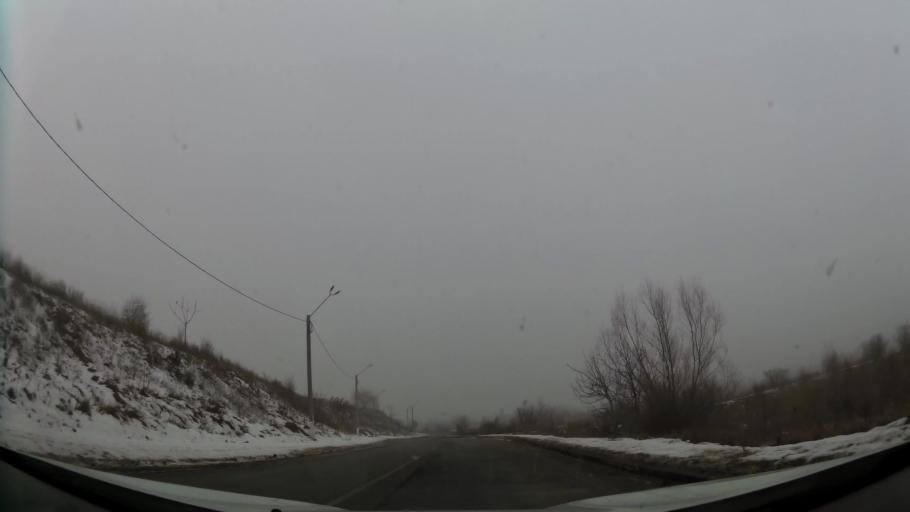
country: RO
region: Ilfov
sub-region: Comuna Chiajna
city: Chiajna
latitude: 44.4619
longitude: 25.9932
